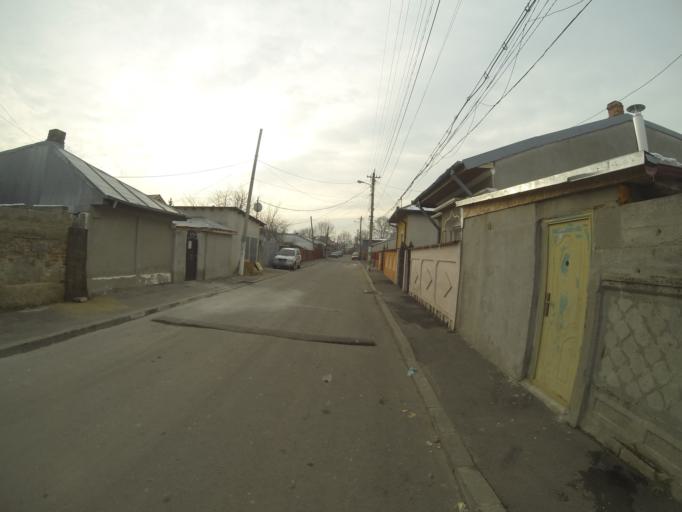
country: RO
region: Bucuresti
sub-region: Municipiul Bucuresti
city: Bucuresti
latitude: 44.3972
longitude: 26.0738
